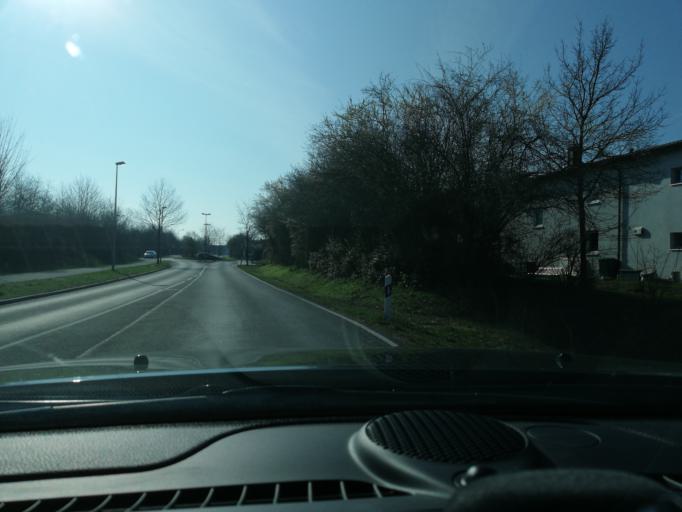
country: DE
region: Bavaria
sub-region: Regierungsbezirk Mittelfranken
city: Hessdorf
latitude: 49.5976
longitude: 10.9455
